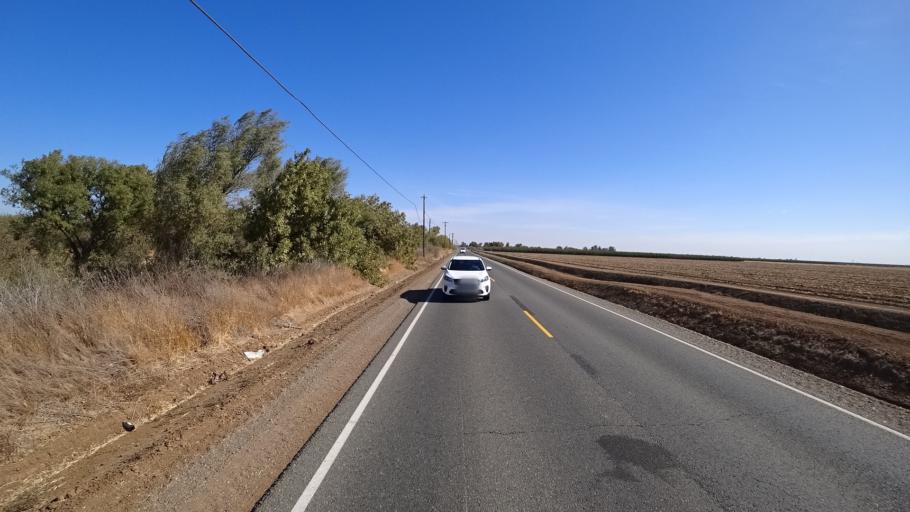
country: US
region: California
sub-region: Yolo County
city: Woodland
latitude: 38.6197
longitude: -121.8373
